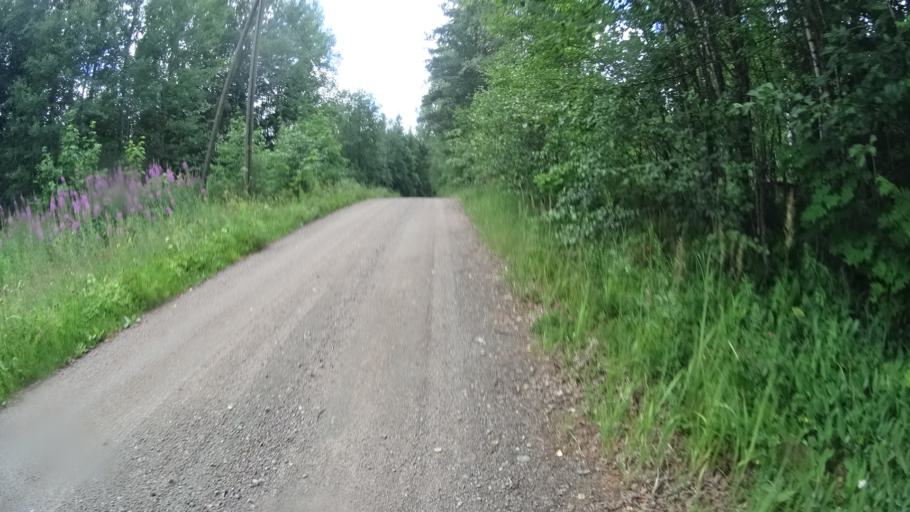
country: FI
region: Uusimaa
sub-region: Helsinki
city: Karkkila
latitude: 60.6063
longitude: 24.1920
